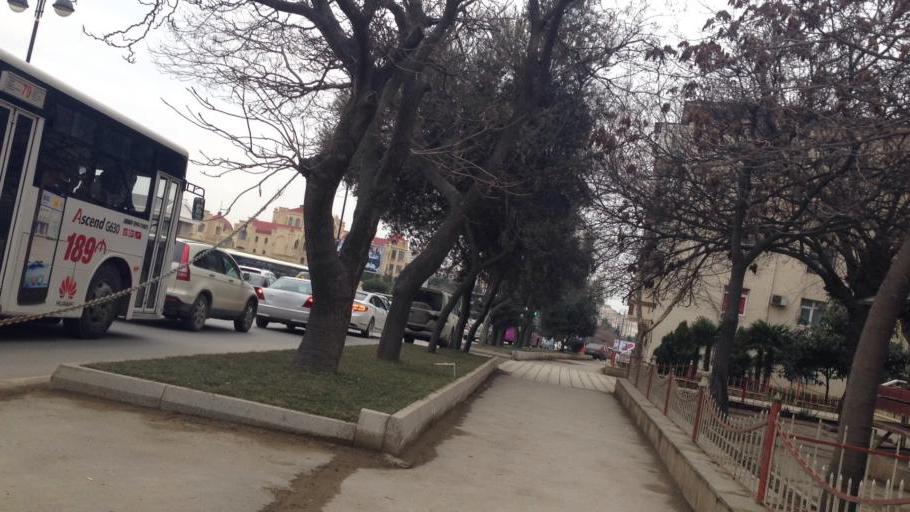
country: AZ
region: Baki
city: Bilajari
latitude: 40.3944
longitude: 49.8190
